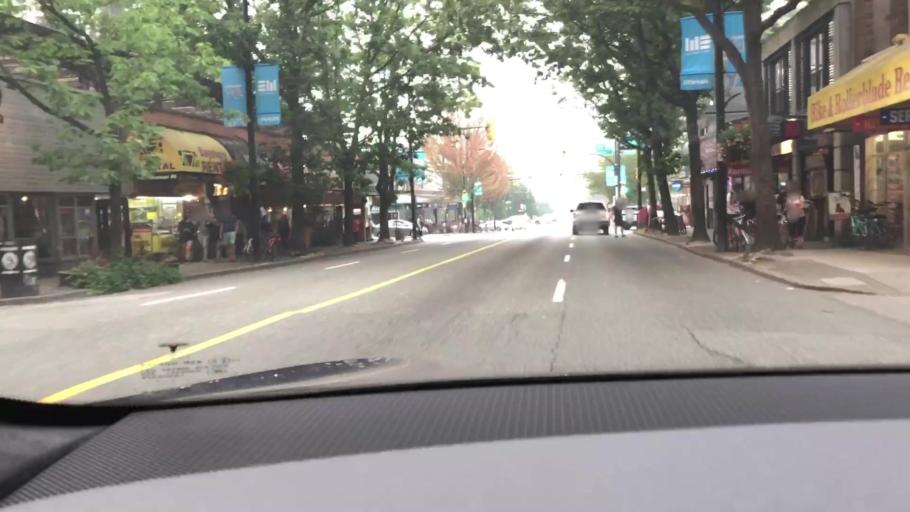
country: CA
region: British Columbia
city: West End
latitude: 49.2918
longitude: -123.1350
